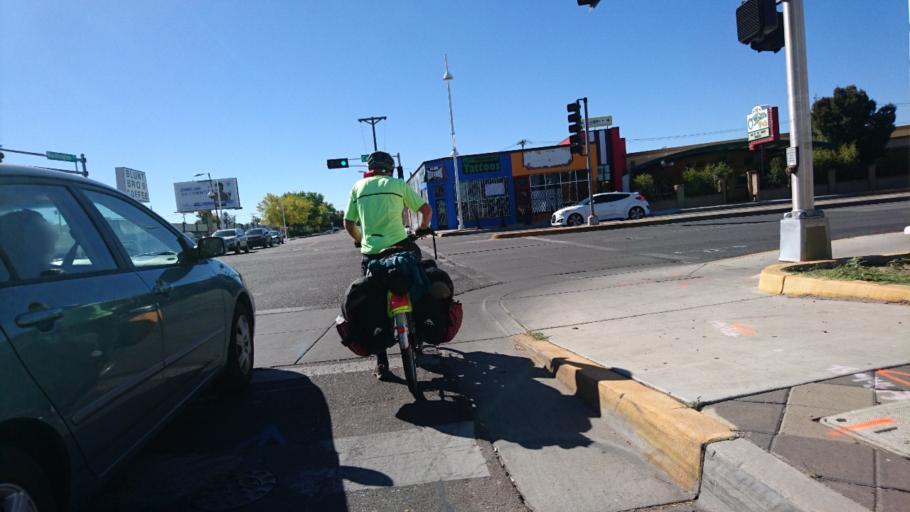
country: US
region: New Mexico
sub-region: Bernalillo County
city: Albuquerque
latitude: 35.0790
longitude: -106.5954
